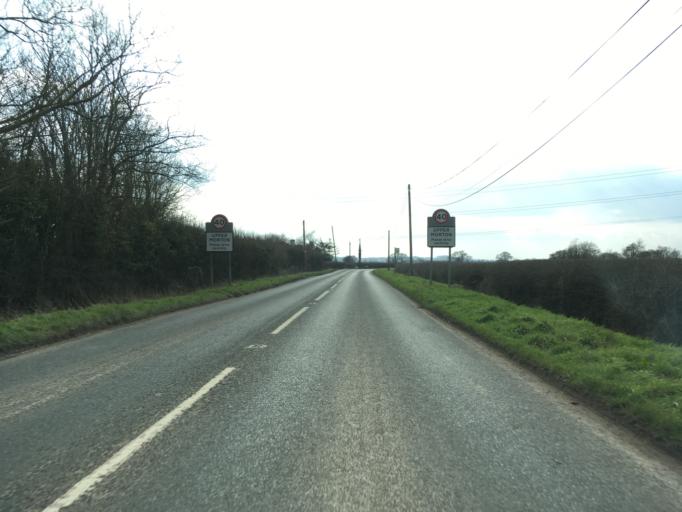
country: GB
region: England
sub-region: South Gloucestershire
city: Thornbury
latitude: 51.6204
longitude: -2.4938
